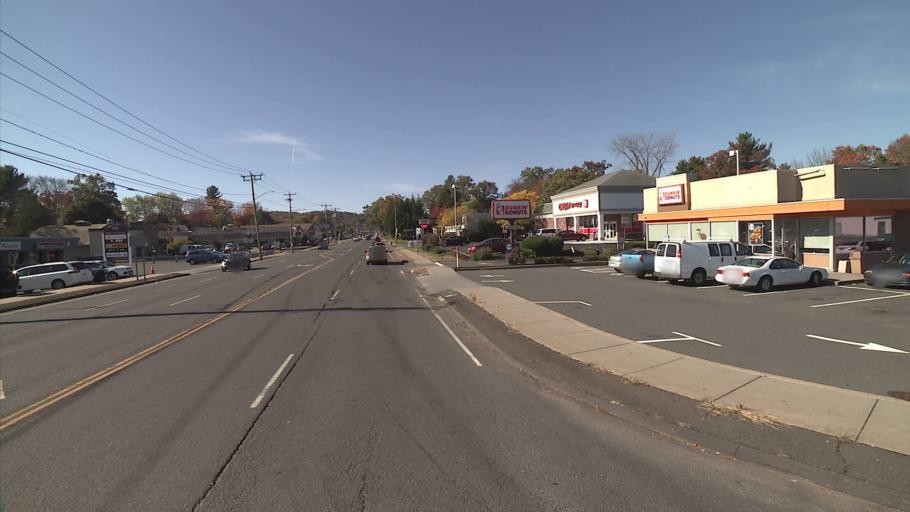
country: US
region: Connecticut
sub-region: Hartford County
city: Bristol
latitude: 41.6934
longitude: -72.9149
